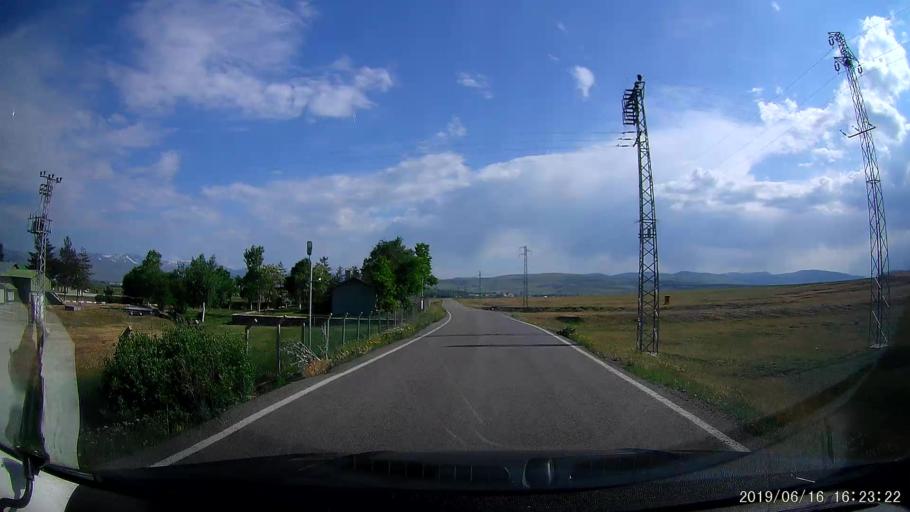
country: TR
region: Erzurum
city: Ilica
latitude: 39.9789
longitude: 41.1066
